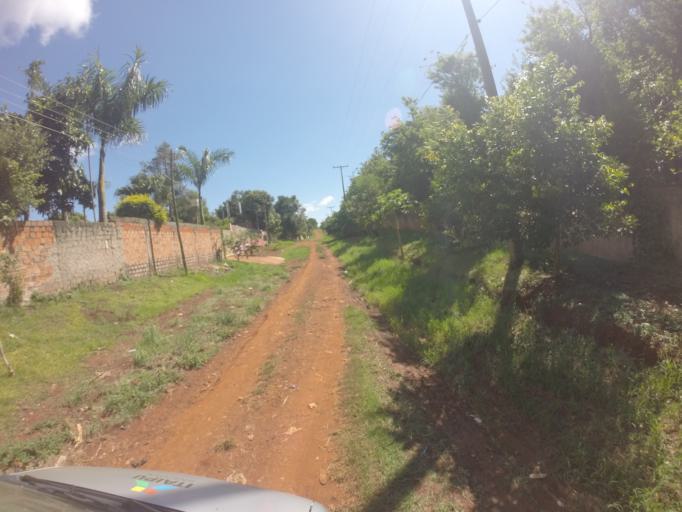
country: PY
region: Alto Parana
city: Ciudad del Este
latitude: -25.4415
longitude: -54.6404
